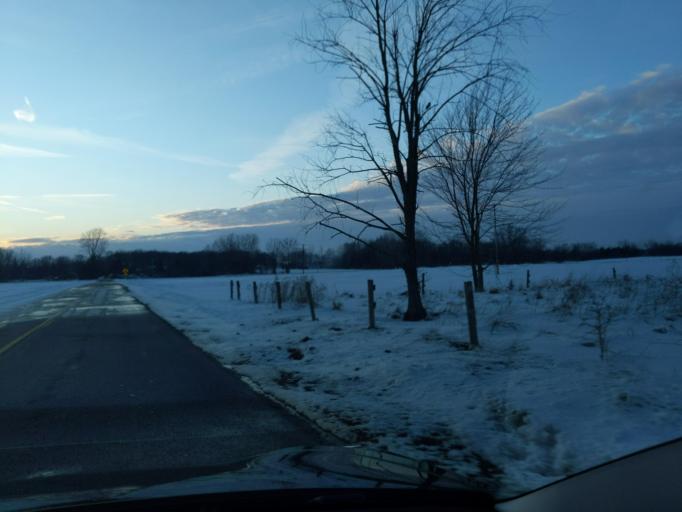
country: US
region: Michigan
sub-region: Ingham County
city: Williamston
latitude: 42.5775
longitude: -84.2949
